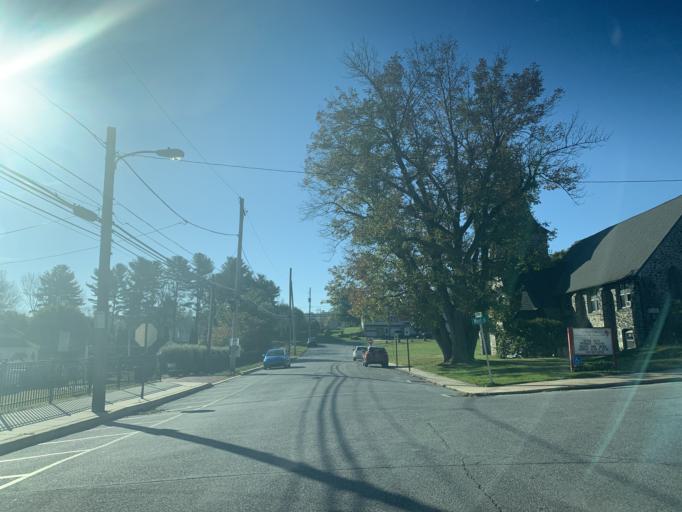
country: US
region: Pennsylvania
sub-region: Chester County
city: Parkesburg
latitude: 39.9579
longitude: -75.9189
